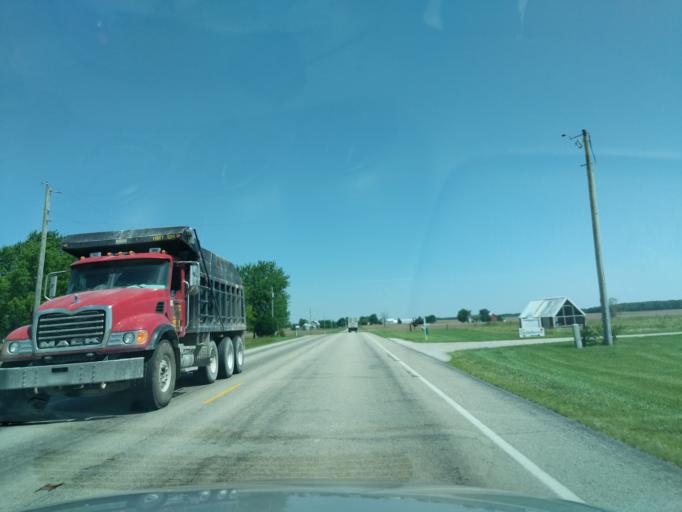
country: US
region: Indiana
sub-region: Huntington County
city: Huntington
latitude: 40.9629
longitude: -85.4712
